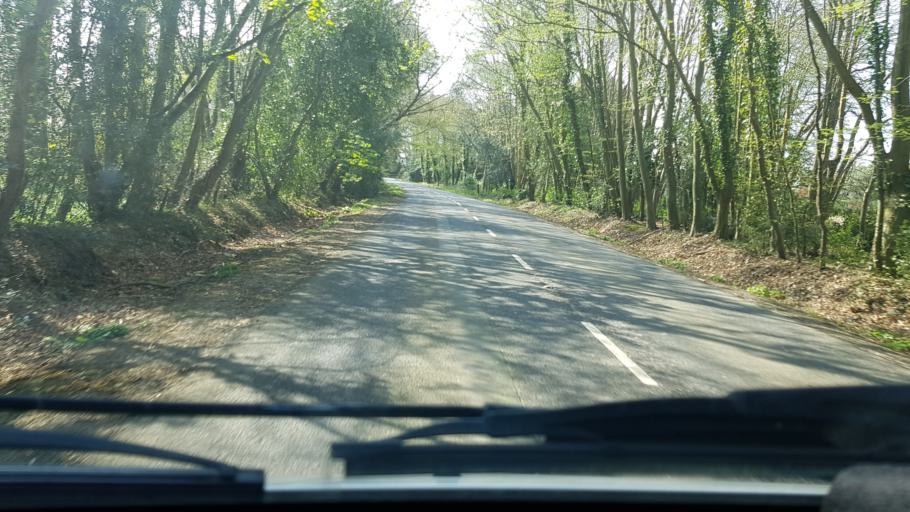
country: GB
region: England
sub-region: West Sussex
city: Chichester
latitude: 50.8515
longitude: -0.8096
